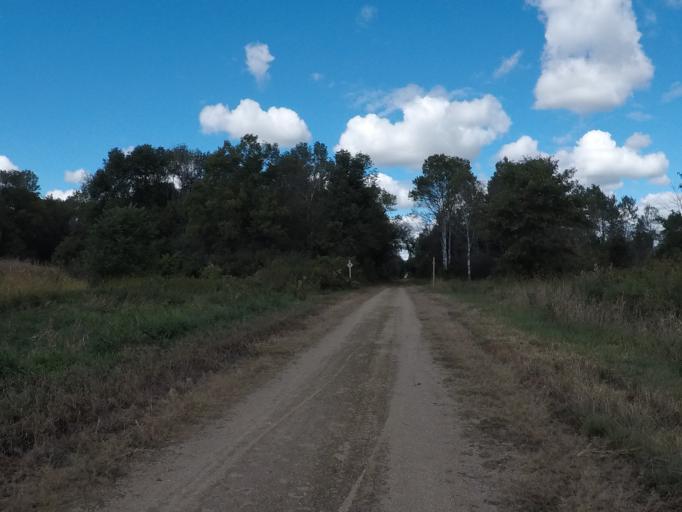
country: US
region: Wisconsin
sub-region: Richland County
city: Richland Center
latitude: 43.3003
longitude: -90.3355
